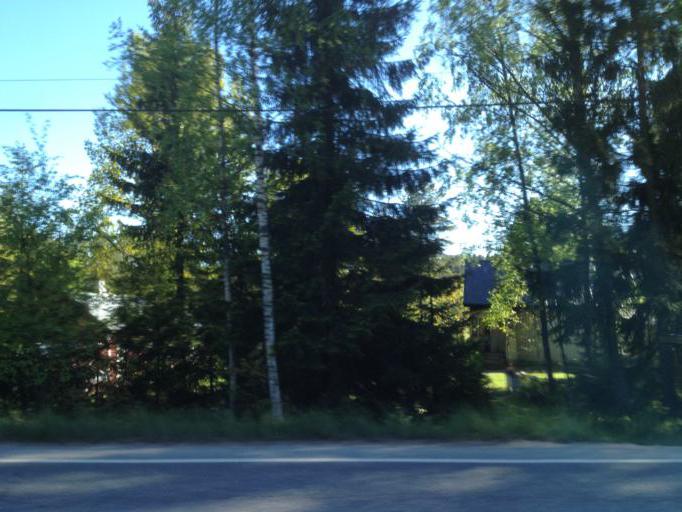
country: FI
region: Uusimaa
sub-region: Helsinki
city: Espoo
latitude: 60.2434
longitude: 24.5795
